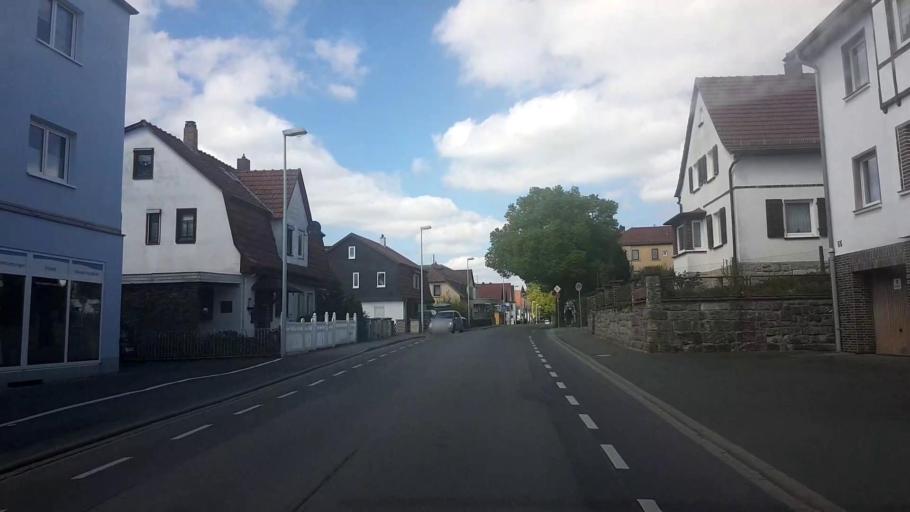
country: DE
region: Bavaria
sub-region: Upper Franconia
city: Niederfullbach
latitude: 50.2348
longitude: 10.9790
